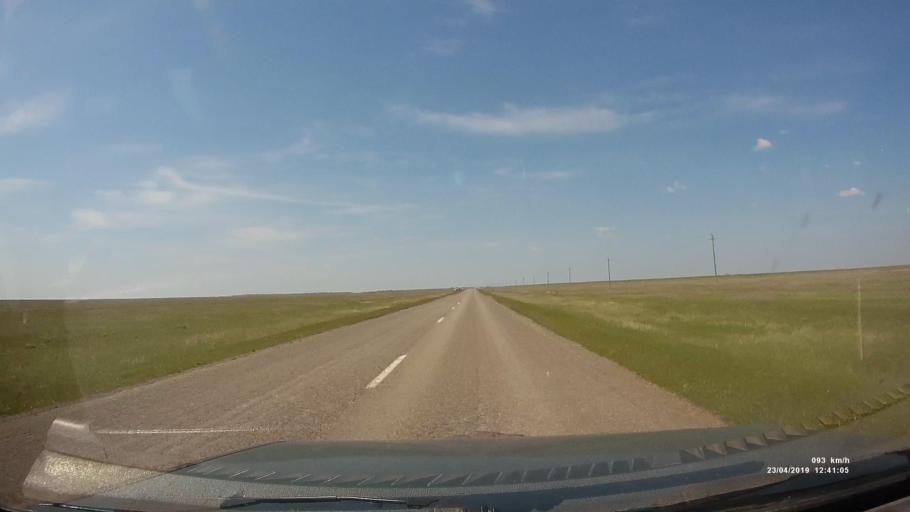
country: RU
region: Kalmykiya
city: Yashalta
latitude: 46.4453
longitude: 42.6867
